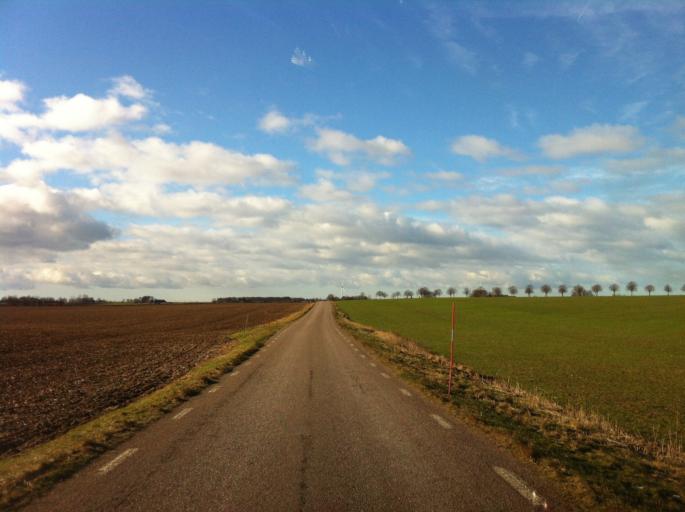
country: SE
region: Skane
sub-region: Svalovs Kommun
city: Svaloev
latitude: 55.9358
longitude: 13.0146
